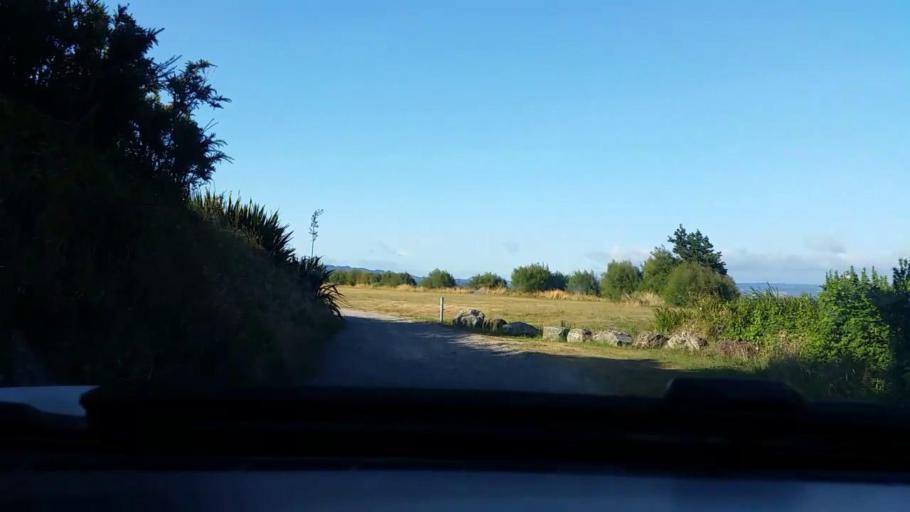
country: NZ
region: Bay of Plenty
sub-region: Rotorua District
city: Rotorua
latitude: -38.0796
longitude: 176.3224
